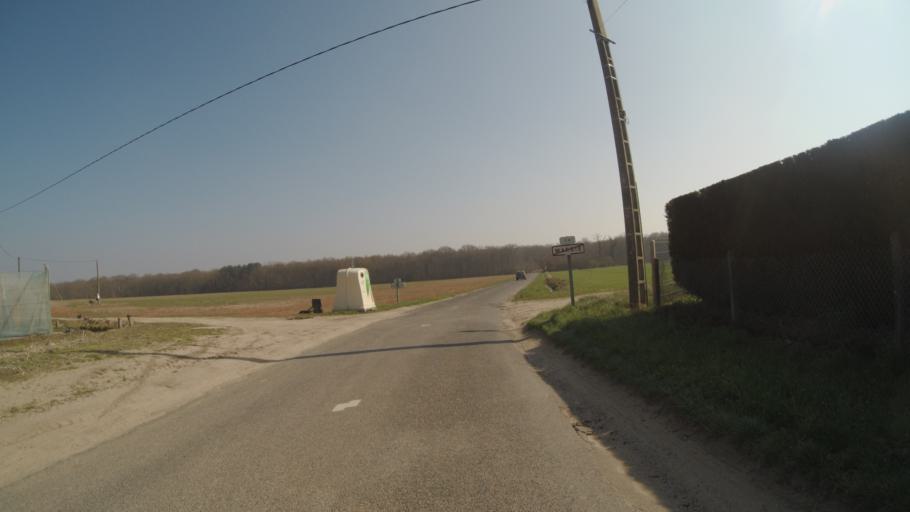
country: FR
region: Centre
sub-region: Departement du Loiret
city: Vennecy
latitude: 47.9210
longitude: 2.0501
